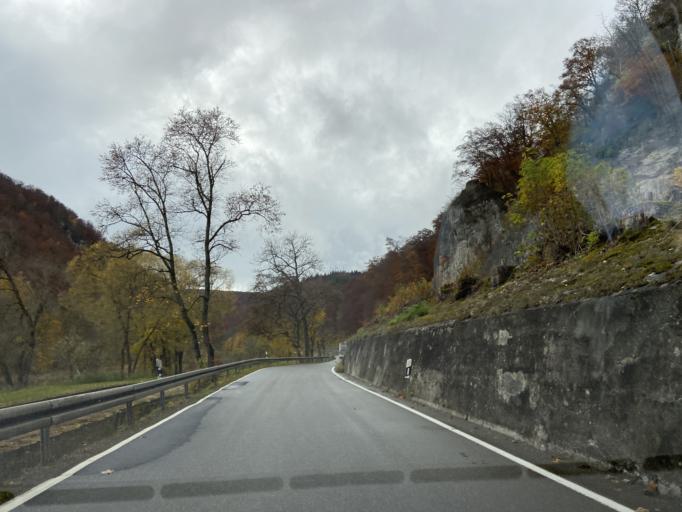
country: DE
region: Baden-Wuerttemberg
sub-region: Tuebingen Region
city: Stetten am Kalten Markt
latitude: 48.0832
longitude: 9.0905
